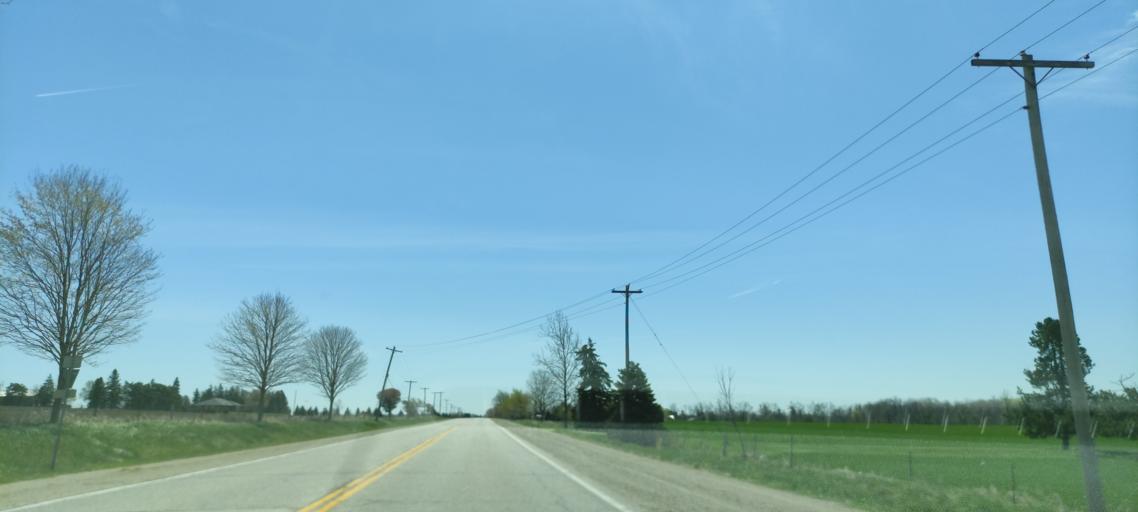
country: CA
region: Ontario
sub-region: Wellington County
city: Guelph
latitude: 43.6035
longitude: -80.3280
